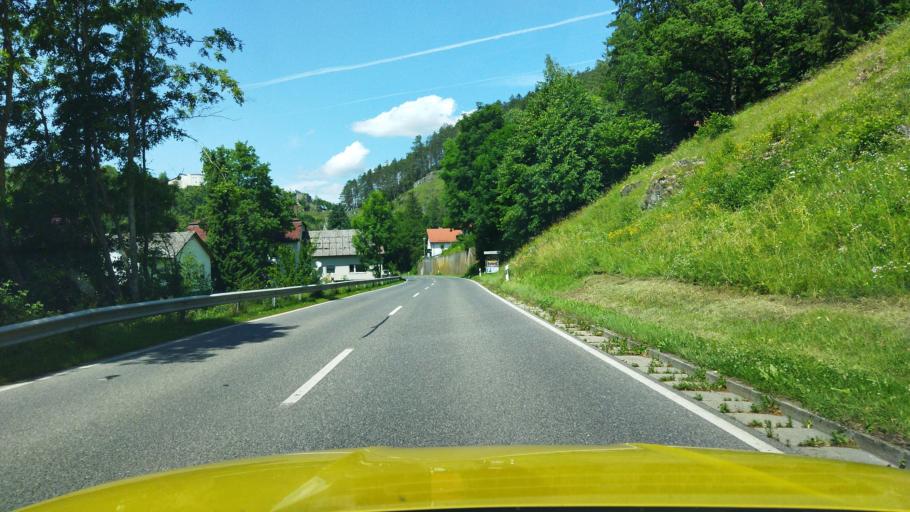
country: DE
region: Bavaria
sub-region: Lower Bavaria
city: Riedenburg
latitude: 48.9537
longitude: 11.6824
